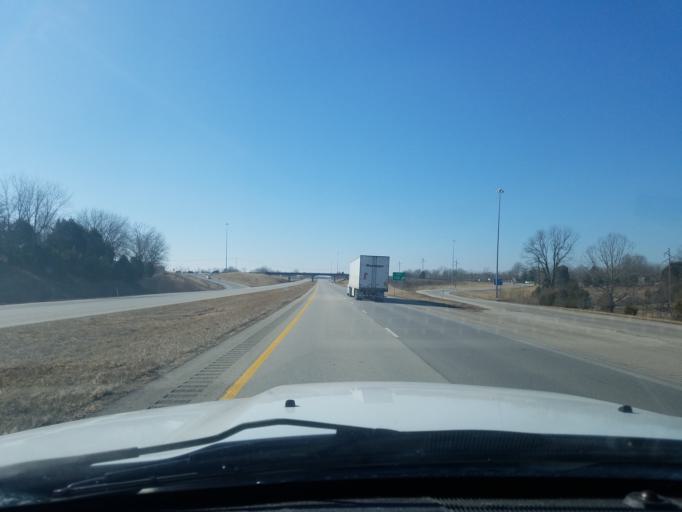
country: US
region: Kentucky
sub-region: Grayson County
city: Leitchfield
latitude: 37.4907
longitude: -86.2051
